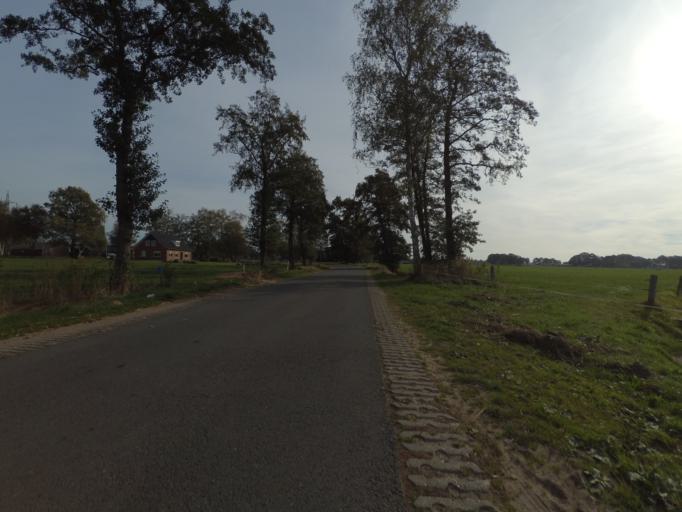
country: NL
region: Overijssel
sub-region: Gemeente Raalte
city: Raalte
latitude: 52.3687
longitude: 6.3358
